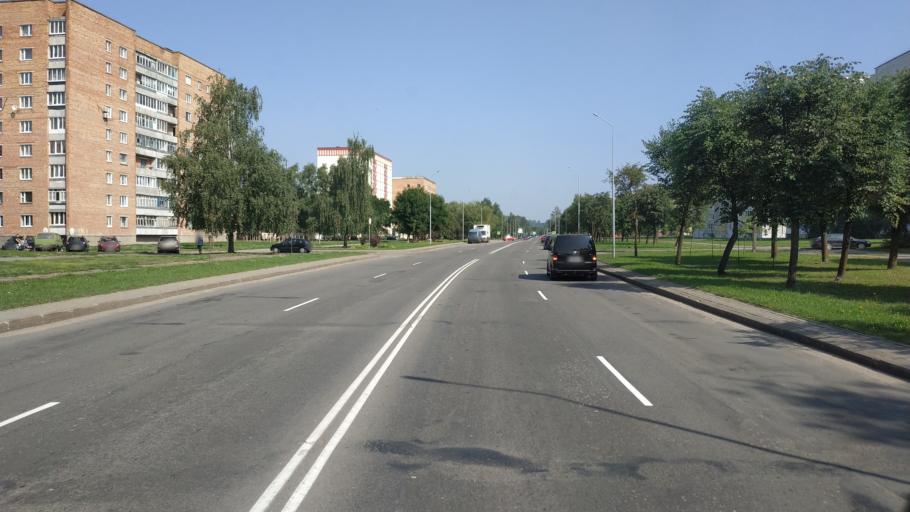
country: BY
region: Mogilev
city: Buynichy
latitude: 53.8680
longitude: 30.3141
